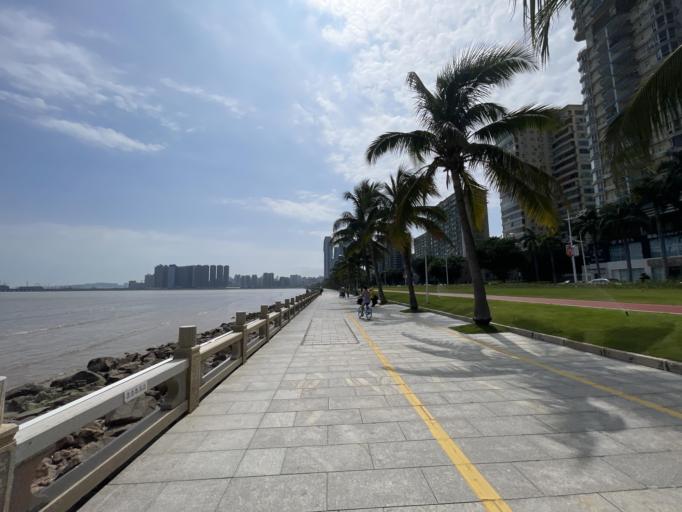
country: CN
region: Guangdong
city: Jida
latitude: 22.2306
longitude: 113.5599
